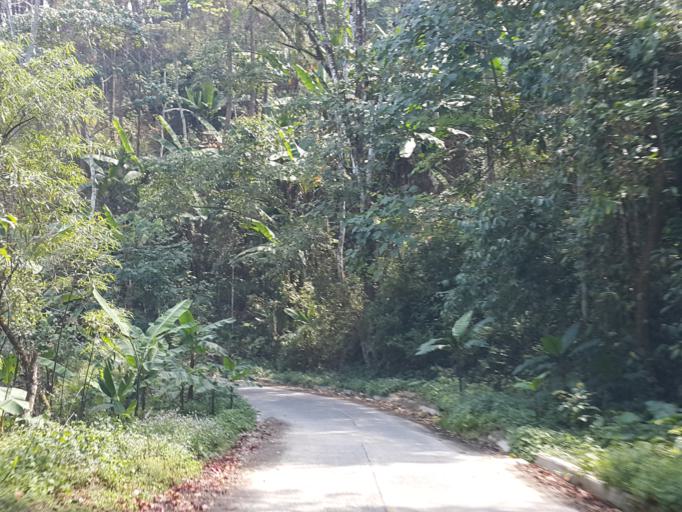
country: TH
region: Chiang Mai
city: Mae On
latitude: 18.8550
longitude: 99.3627
